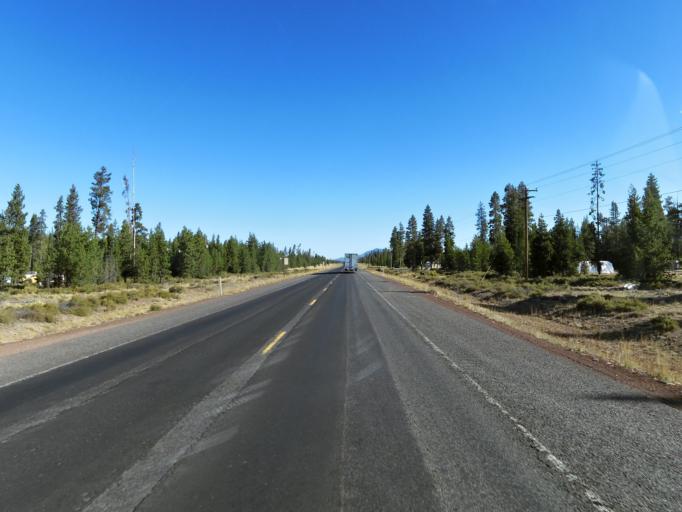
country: US
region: Oregon
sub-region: Deschutes County
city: La Pine
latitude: 43.1377
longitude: -121.8015
